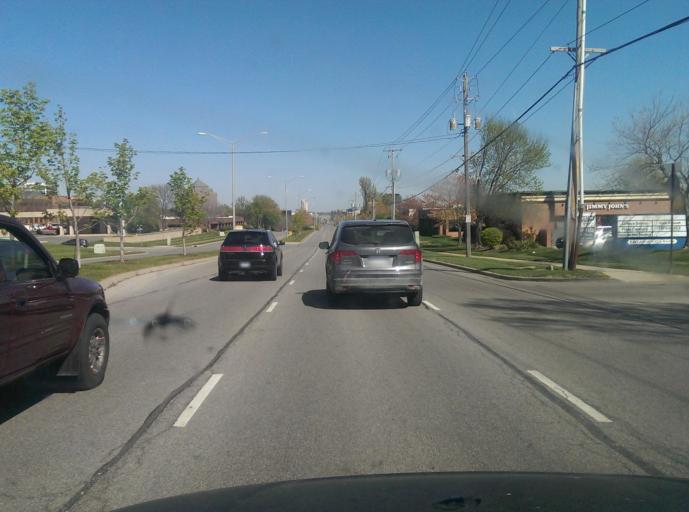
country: US
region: Kansas
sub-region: Johnson County
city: Lenexa
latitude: 38.9274
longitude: -94.6849
